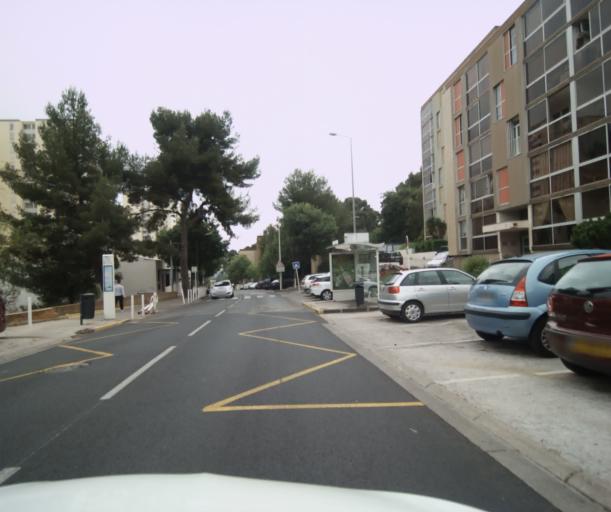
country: FR
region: Provence-Alpes-Cote d'Azur
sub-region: Departement du Var
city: Ollioules
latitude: 43.1334
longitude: 5.8819
